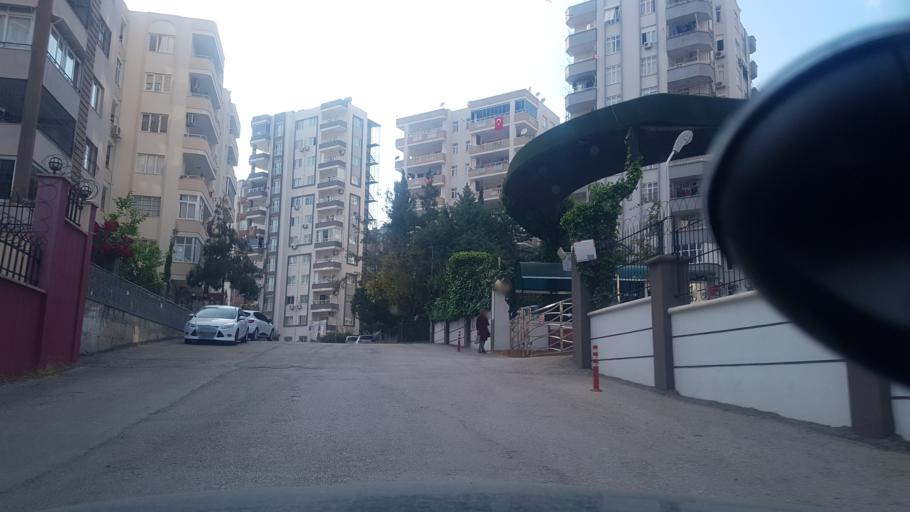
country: TR
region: Adana
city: Seyhan
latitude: 37.0466
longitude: 35.2761
